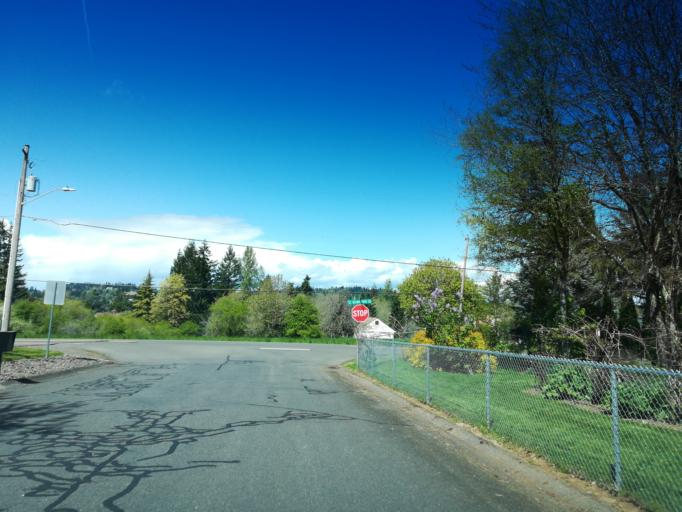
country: US
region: Oregon
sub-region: Clackamas County
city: Damascus
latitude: 45.4322
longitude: -122.4307
